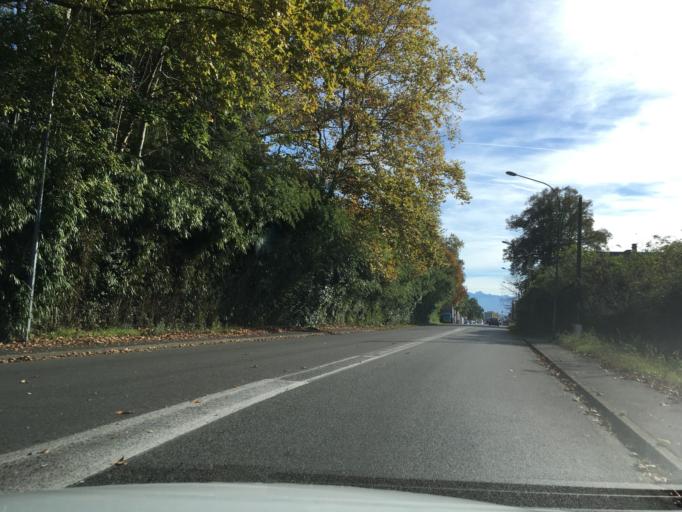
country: FR
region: Aquitaine
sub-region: Departement des Pyrenees-Atlantiques
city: Lons
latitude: 43.3380
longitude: -0.3798
